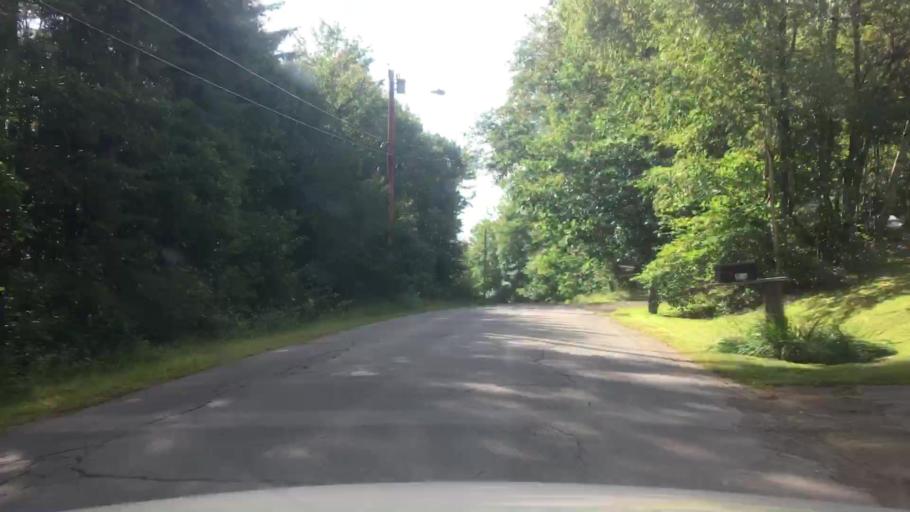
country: US
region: Maine
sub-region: Kennebec County
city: Gardiner
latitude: 44.1659
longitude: -69.8118
